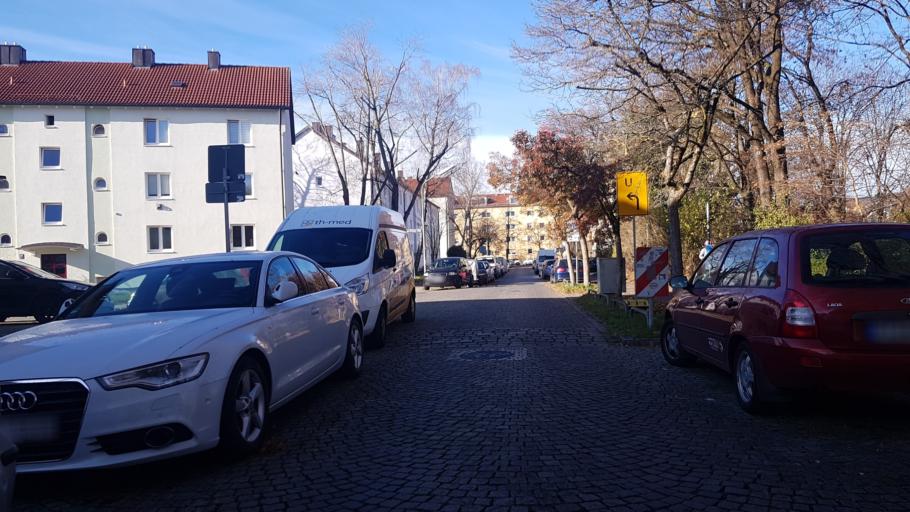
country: DE
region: Bavaria
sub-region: Upper Bavaria
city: Karlsfeld
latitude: 48.1774
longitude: 11.5106
